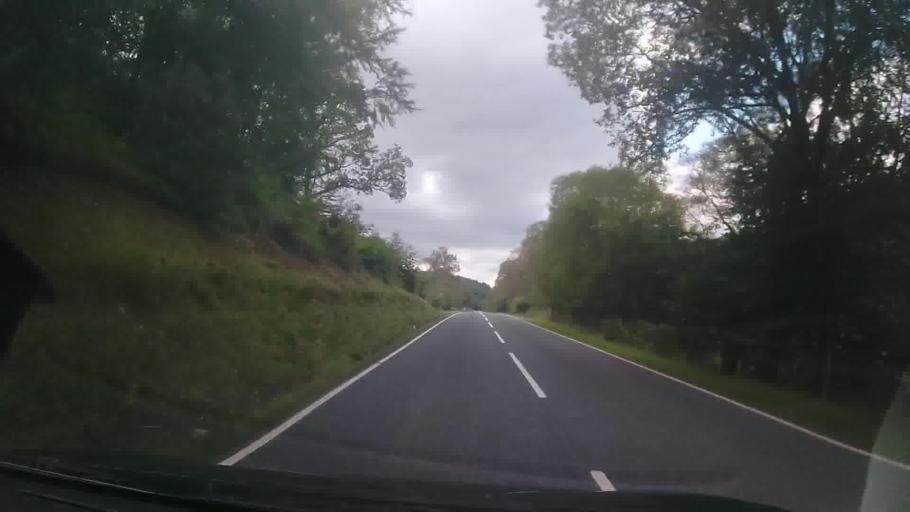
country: GB
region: Scotland
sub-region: Argyll and Bute
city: Garelochhead
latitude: 56.4010
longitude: -5.0209
